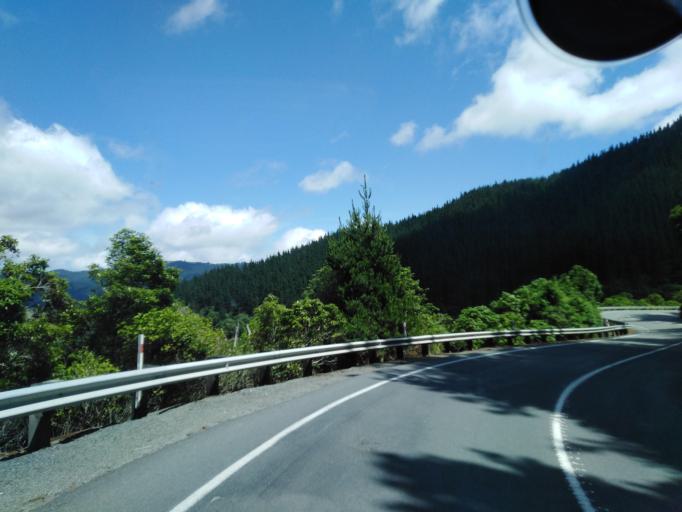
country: NZ
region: Nelson
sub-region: Nelson City
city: Nelson
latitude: -41.2291
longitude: 173.4216
